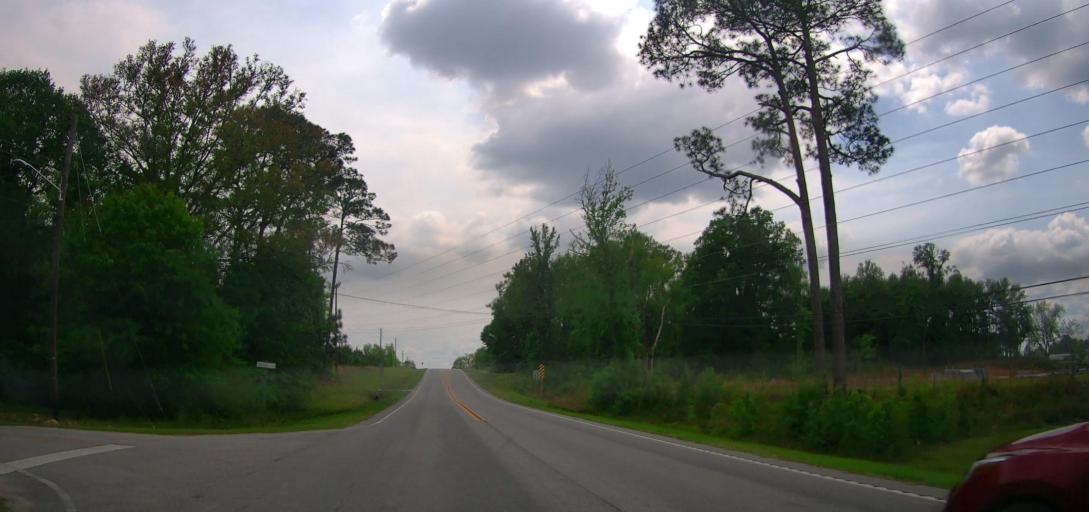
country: US
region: Georgia
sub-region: Treutlen County
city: Soperton
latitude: 32.3630
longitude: -82.5952
